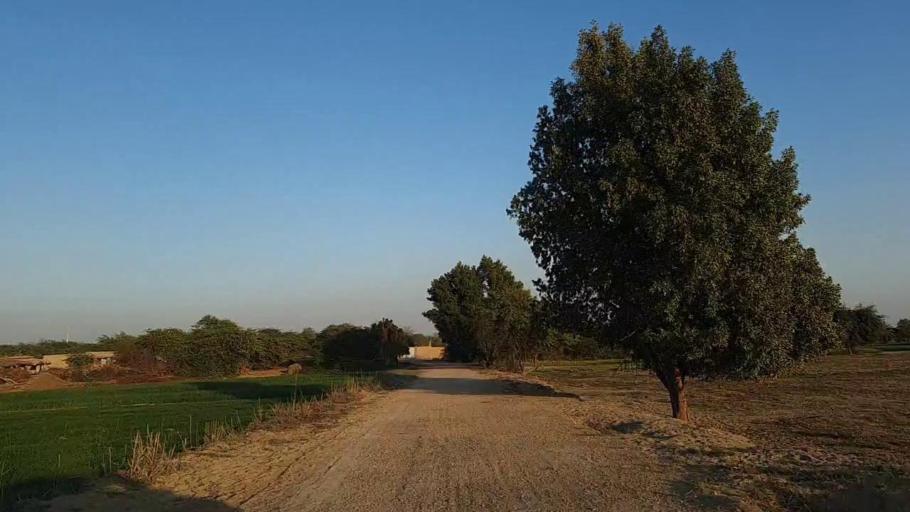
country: PK
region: Sindh
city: Jam Sahib
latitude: 26.3399
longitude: 68.6185
